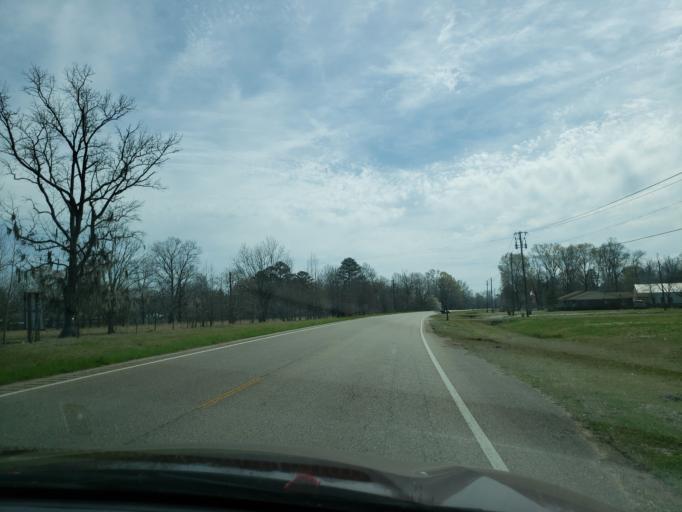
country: US
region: Alabama
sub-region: Dallas County
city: Selma
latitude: 32.4683
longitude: -87.0971
